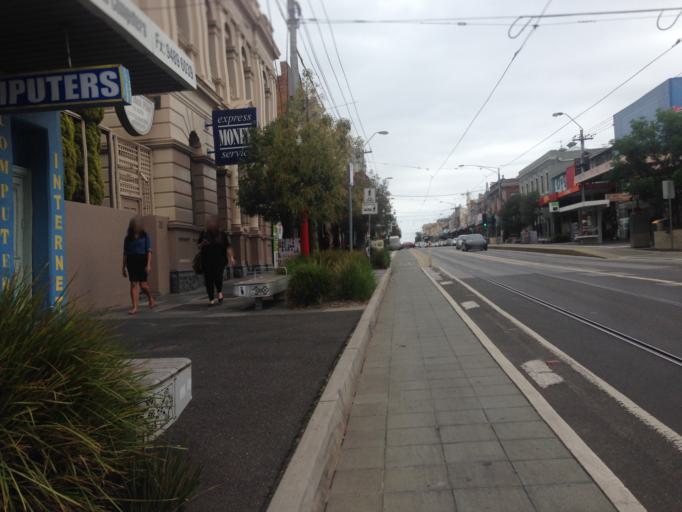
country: AU
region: Victoria
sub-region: Darebin
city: Northcote
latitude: -37.7708
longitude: 144.9988
